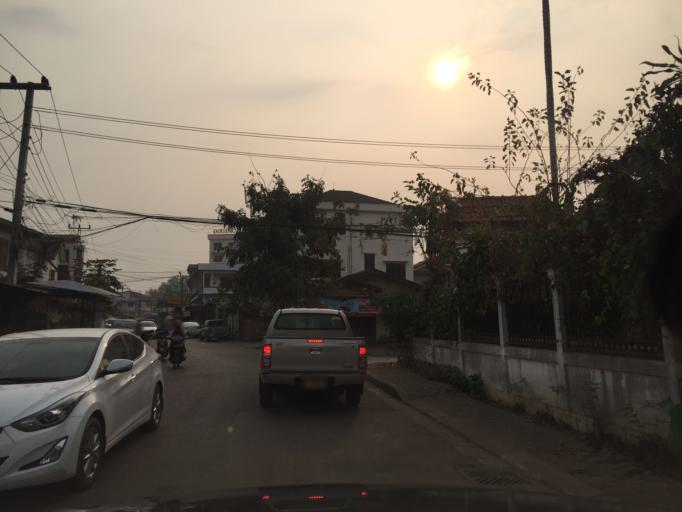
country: LA
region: Vientiane
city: Vientiane
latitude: 17.9744
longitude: 102.6131
